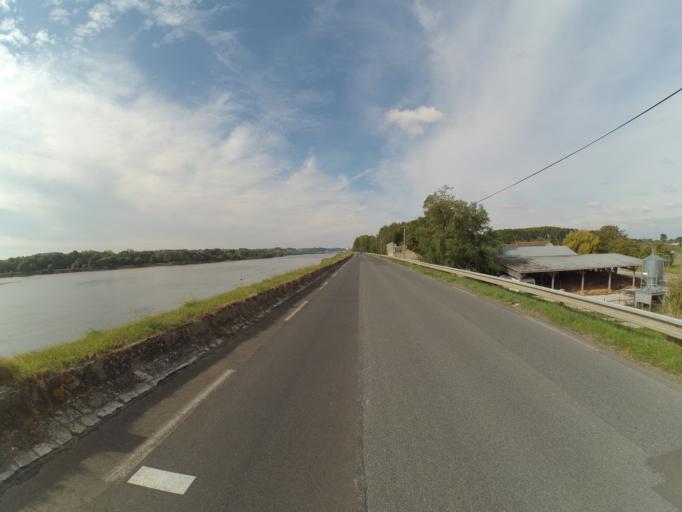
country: FR
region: Pays de la Loire
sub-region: Departement de Maine-et-Loire
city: Villebernier
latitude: 47.2486
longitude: -0.0098
